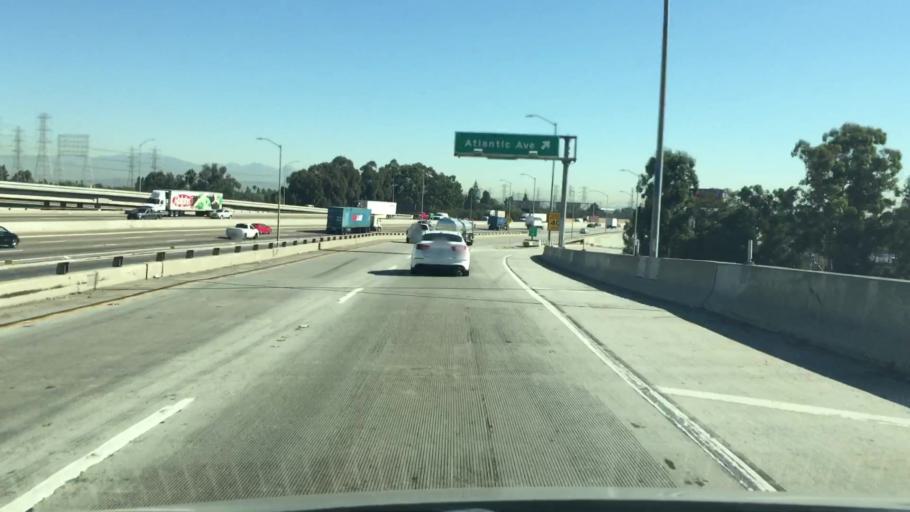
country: US
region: California
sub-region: Los Angeles County
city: East Rancho Dominguez
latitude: 33.8760
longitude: -118.1904
